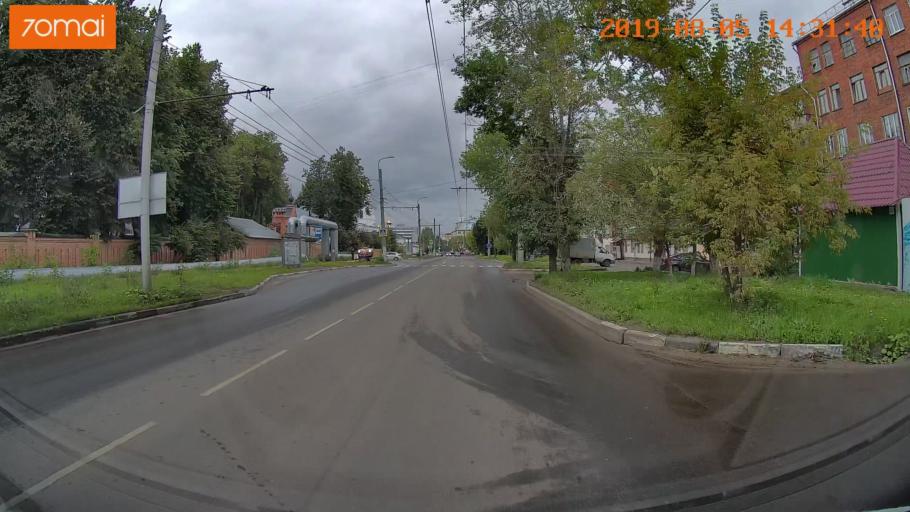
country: RU
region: Ivanovo
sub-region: Gorod Ivanovo
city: Ivanovo
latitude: 56.9880
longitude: 40.9990
